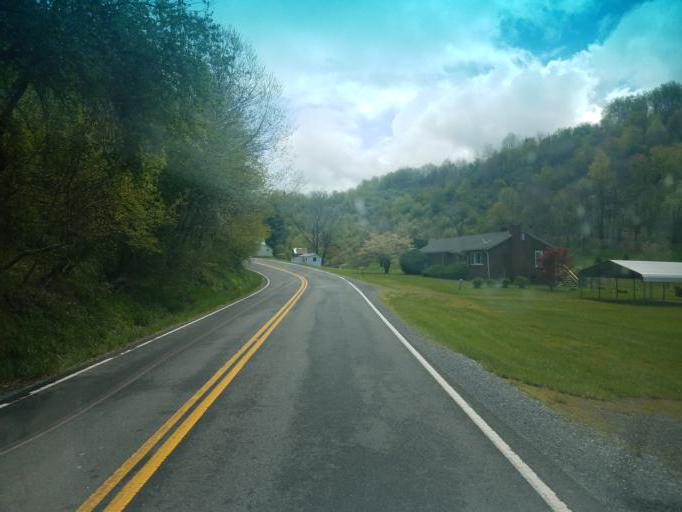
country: US
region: Virginia
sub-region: Smyth County
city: Atkins
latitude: 36.9852
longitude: -81.3953
